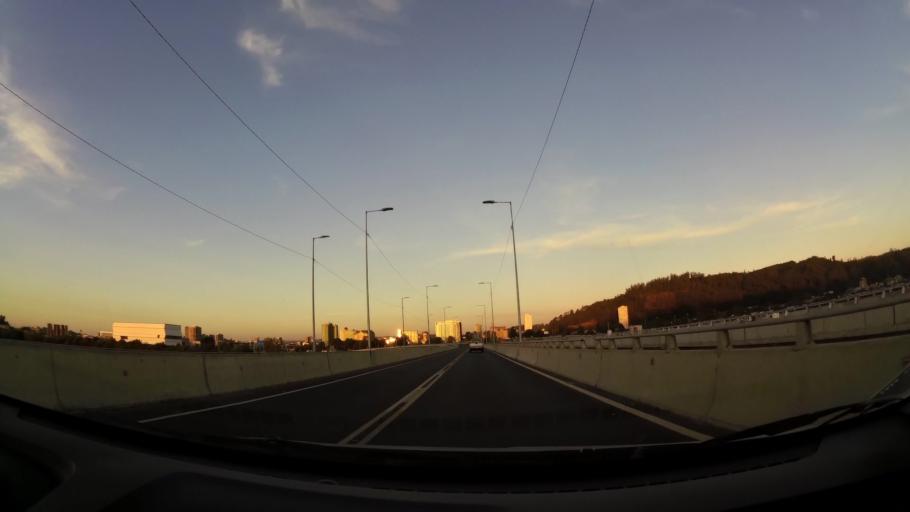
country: CL
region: Biobio
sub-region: Provincia de Concepcion
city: Concepcion
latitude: -36.8386
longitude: -73.0668
